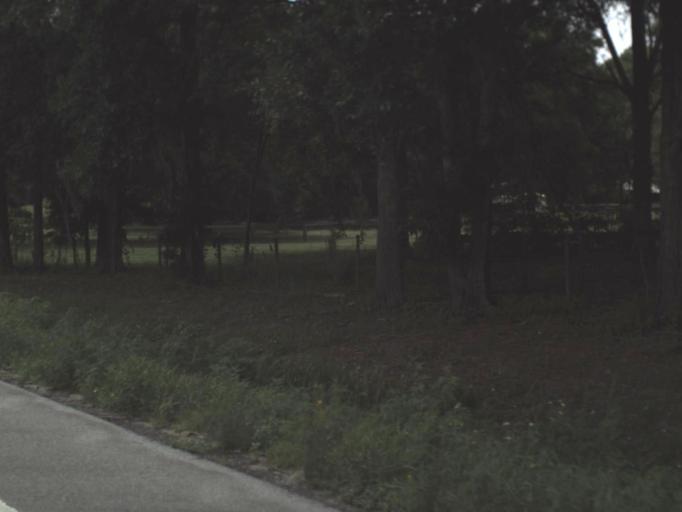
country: US
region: Florida
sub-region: Madison County
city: Madison
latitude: 30.4723
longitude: -83.3229
